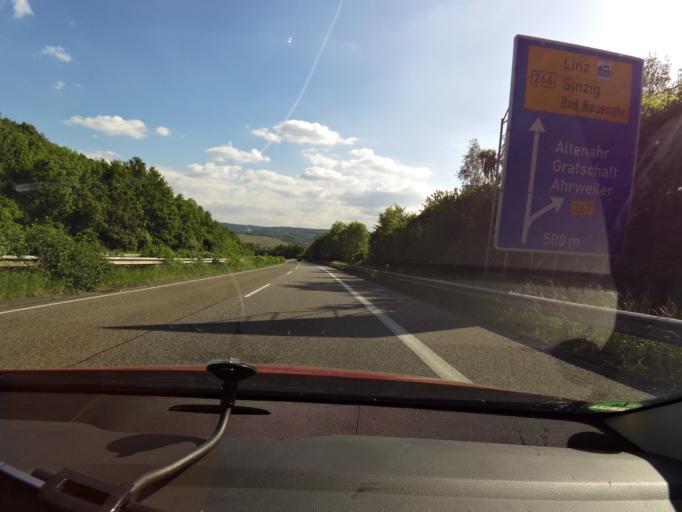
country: DE
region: Rheinland-Pfalz
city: Bad Neuenahr-Ahrweiler
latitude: 50.5597
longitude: 7.1168
